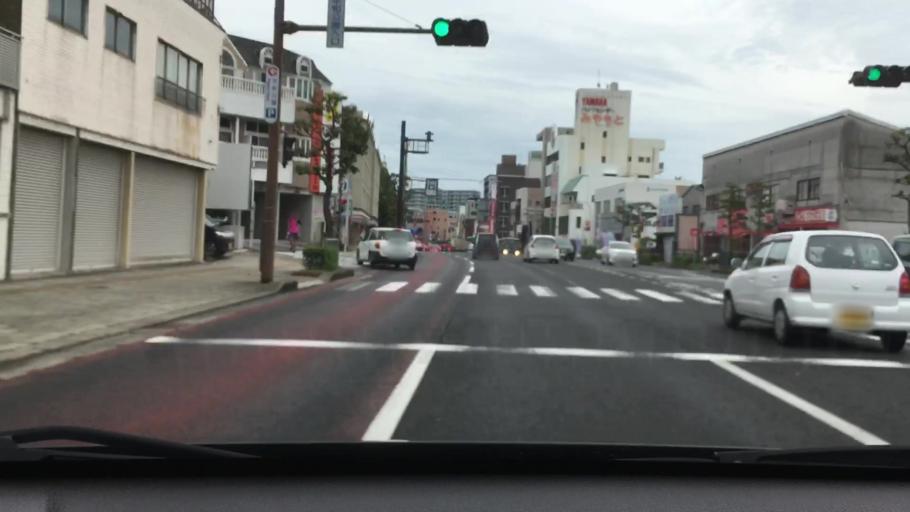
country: JP
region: Nagasaki
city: Nagasaki-shi
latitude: 32.7760
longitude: 129.8621
